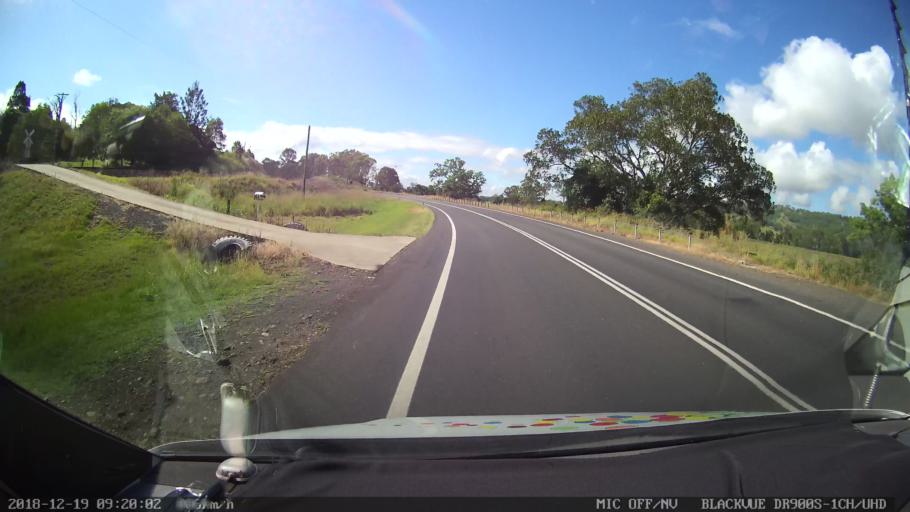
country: AU
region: New South Wales
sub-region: Kyogle
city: Kyogle
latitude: -28.5676
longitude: 152.9777
